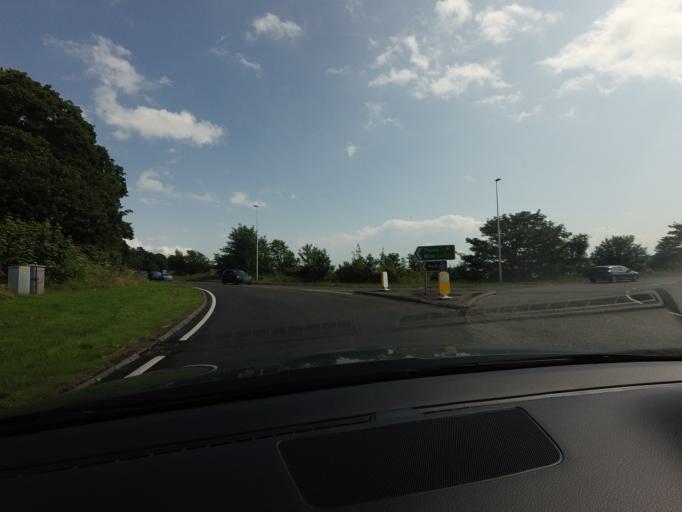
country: GB
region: Scotland
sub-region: Highland
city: Evanton
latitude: 57.6283
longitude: -4.3675
